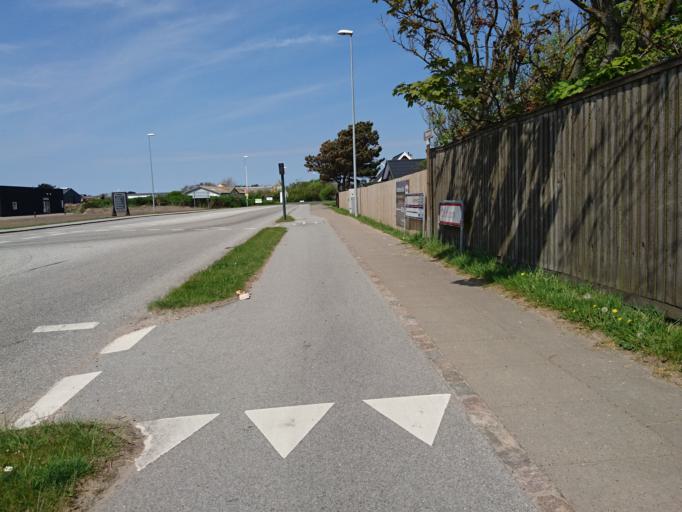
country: DK
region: North Denmark
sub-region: Frederikshavn Kommune
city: Skagen
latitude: 57.7269
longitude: 10.5697
